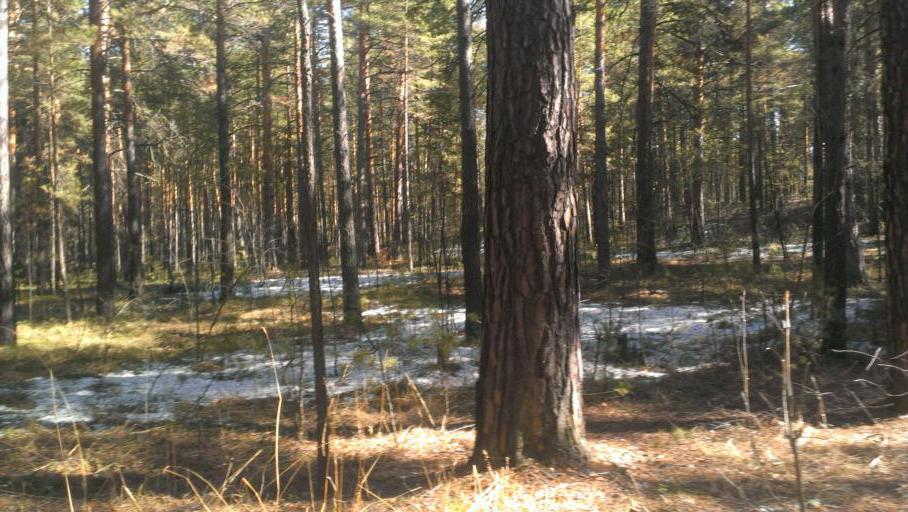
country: RU
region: Altai Krai
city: Yuzhnyy
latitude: 53.2969
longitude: 83.6948
